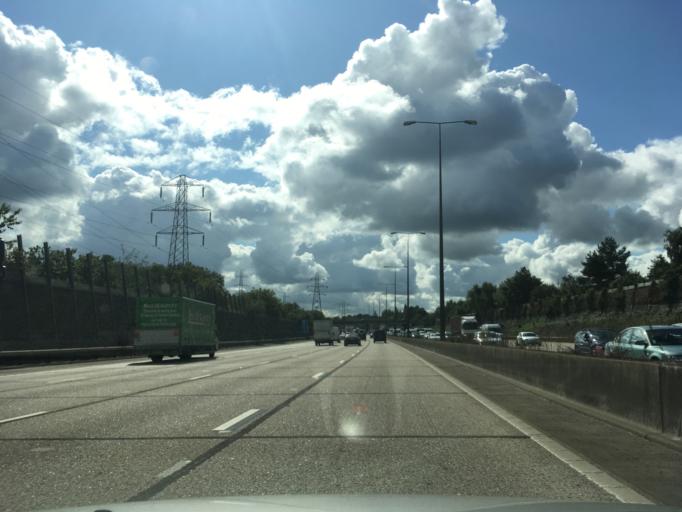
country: GB
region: England
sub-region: Surrey
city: Byfleet
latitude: 51.3429
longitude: -0.4853
